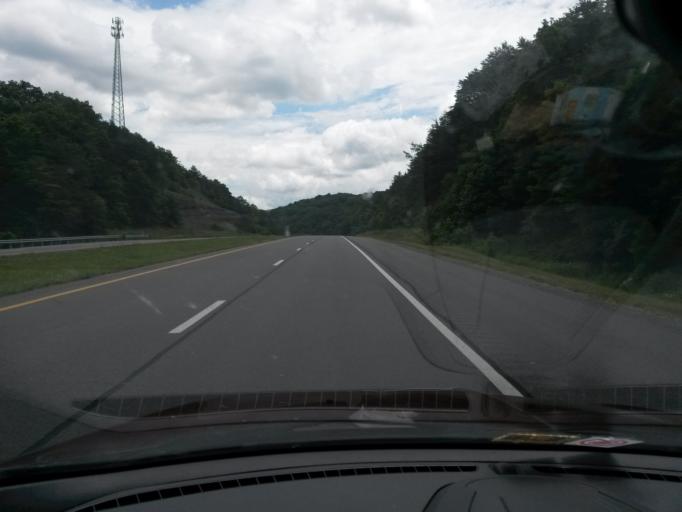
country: US
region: West Virginia
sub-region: Mercer County
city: Athens
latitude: 37.3418
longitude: -80.9790
